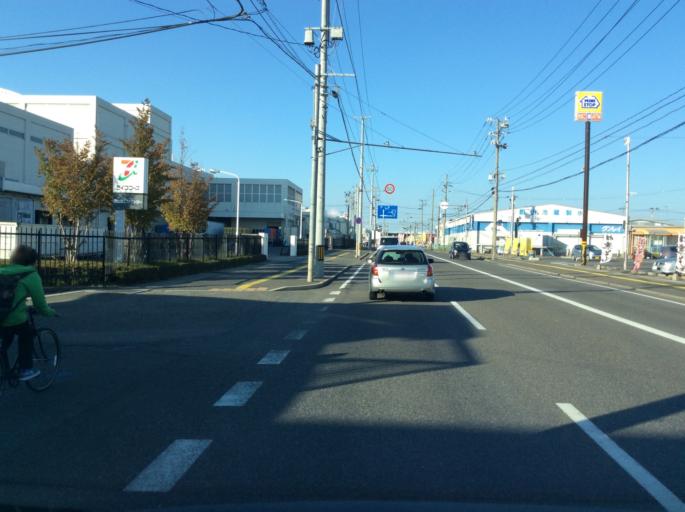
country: JP
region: Fukushima
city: Koriyama
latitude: 37.4076
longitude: 140.3967
